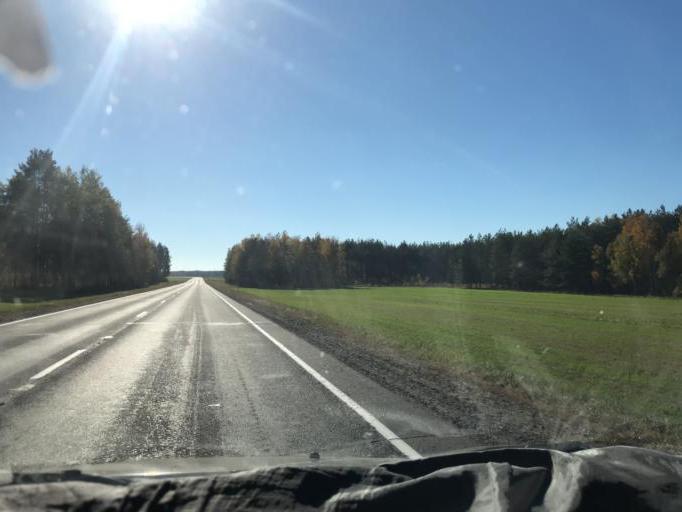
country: BY
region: Gomel
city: Parychy
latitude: 52.8800
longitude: 29.3151
